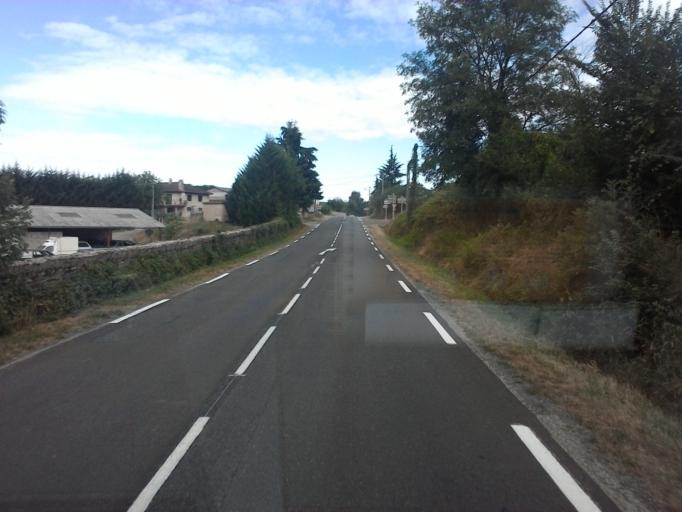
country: FR
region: Rhone-Alpes
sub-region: Departement de l'Ain
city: Saint-Sorlin-en-Bugey
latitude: 45.8931
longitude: 5.3594
